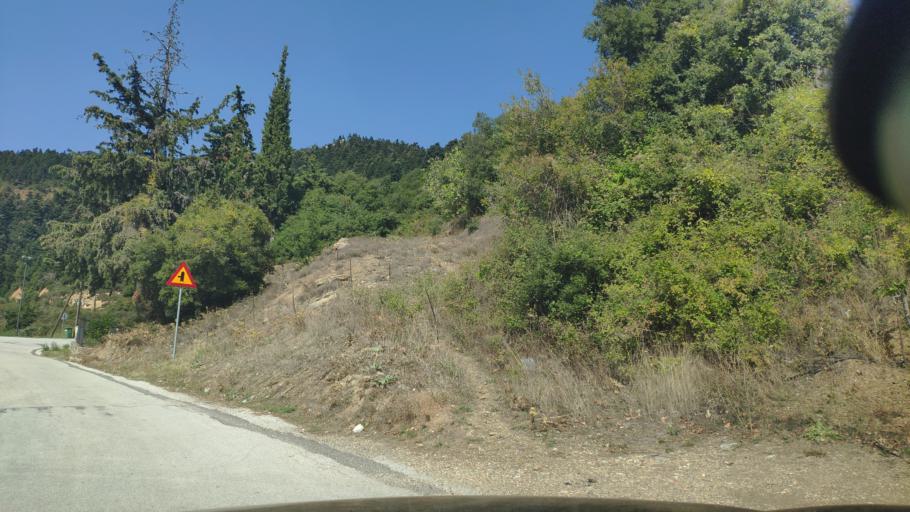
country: GR
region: West Greece
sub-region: Nomos Achaias
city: Aiyira
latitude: 37.8669
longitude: 22.3803
